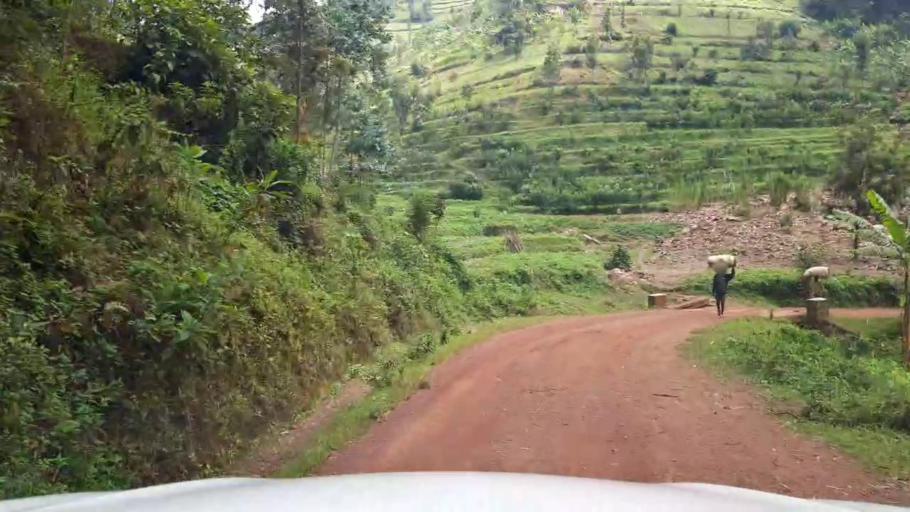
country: UG
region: Western Region
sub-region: Kisoro District
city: Kisoro
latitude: -1.3800
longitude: 29.7940
